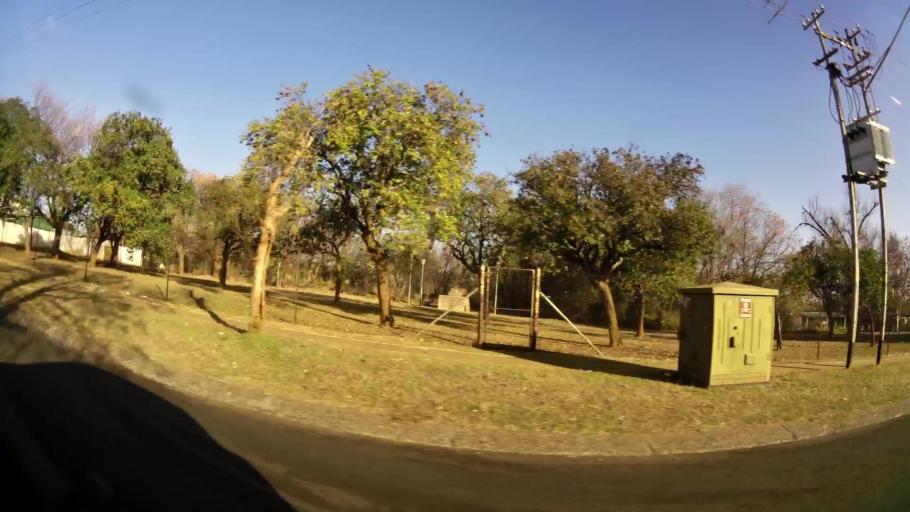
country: ZA
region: Gauteng
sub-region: City of Tshwane Metropolitan Municipality
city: Pretoria
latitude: -25.7049
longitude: 28.2031
